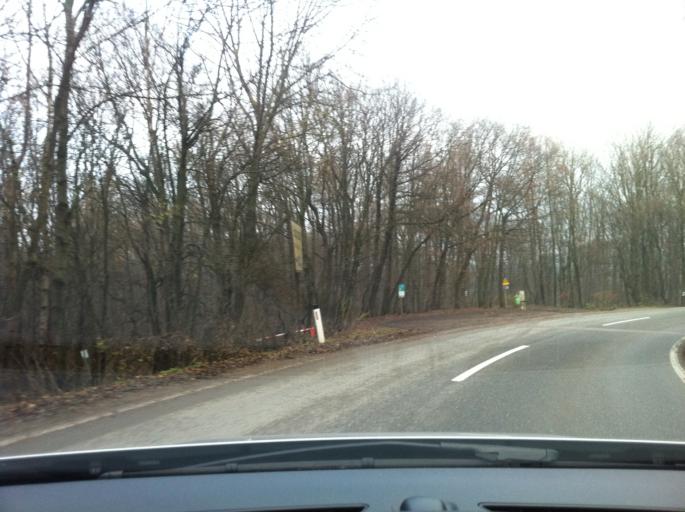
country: AT
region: Lower Austria
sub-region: Politischer Bezirk Wien-Umgebung
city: Mauerbach
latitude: 48.2498
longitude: 16.2449
